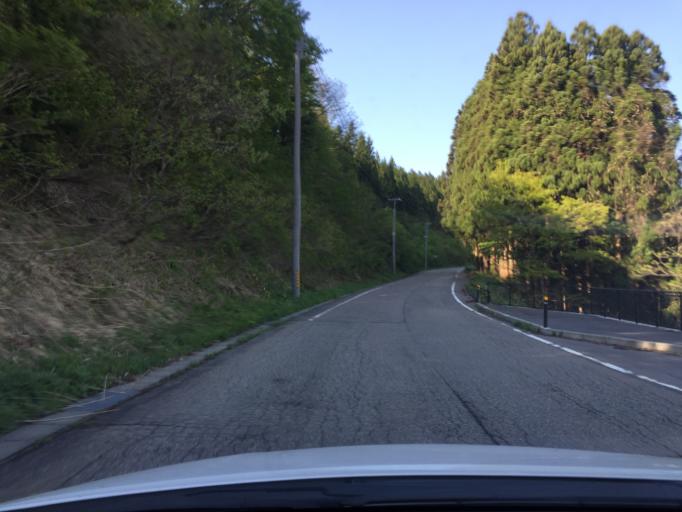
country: JP
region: Fukushima
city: Kitakata
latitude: 37.6890
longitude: 139.7034
